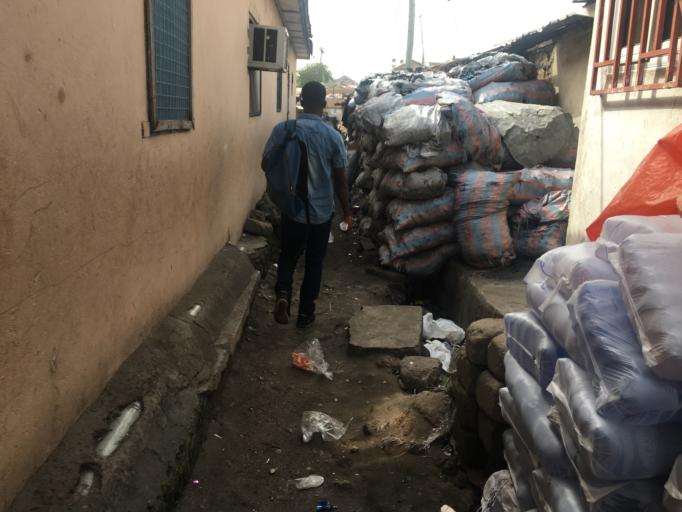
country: GH
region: Greater Accra
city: Accra
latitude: 5.5895
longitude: -0.1923
